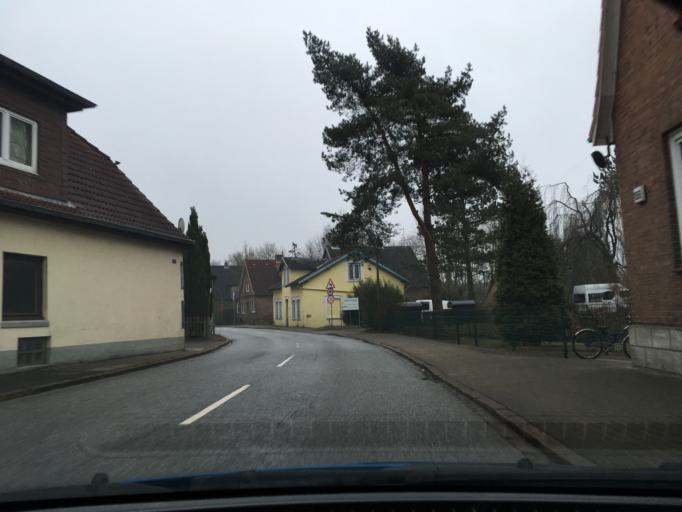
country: DE
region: Hamburg
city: Harburg
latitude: 53.4897
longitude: 9.9370
